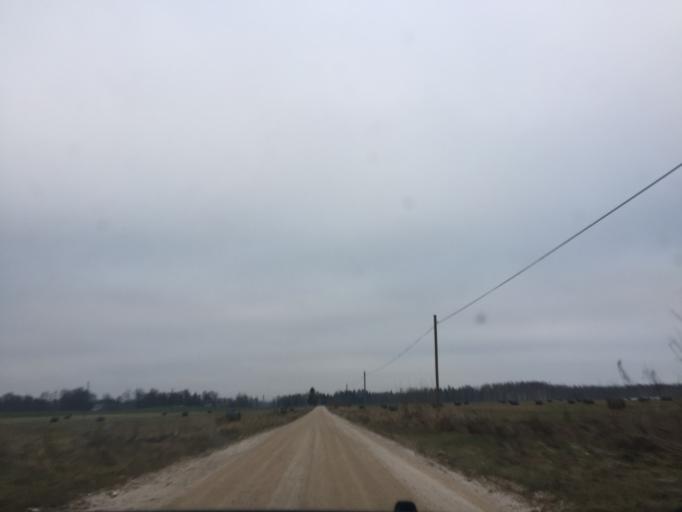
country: LV
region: Raunas
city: Rauna
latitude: 57.3146
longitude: 25.5923
